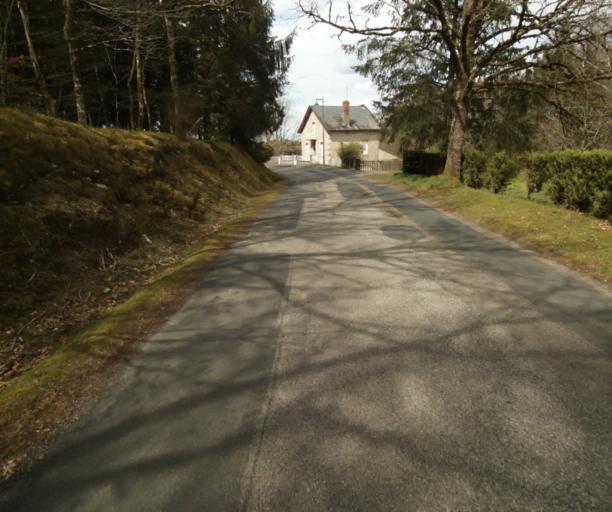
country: FR
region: Limousin
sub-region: Departement de la Correze
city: Laguenne
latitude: 45.2170
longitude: 1.8985
